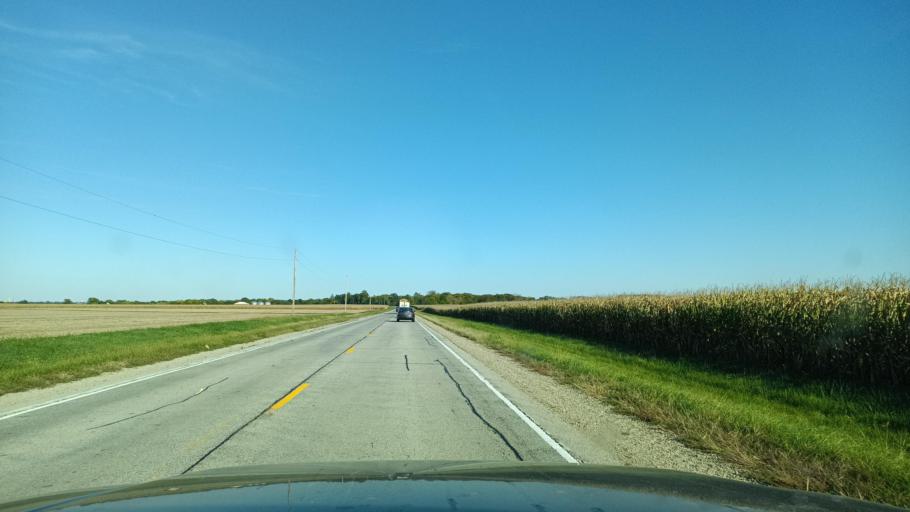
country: US
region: Illinois
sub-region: De Witt County
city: Farmer City
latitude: 40.2238
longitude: -88.7060
